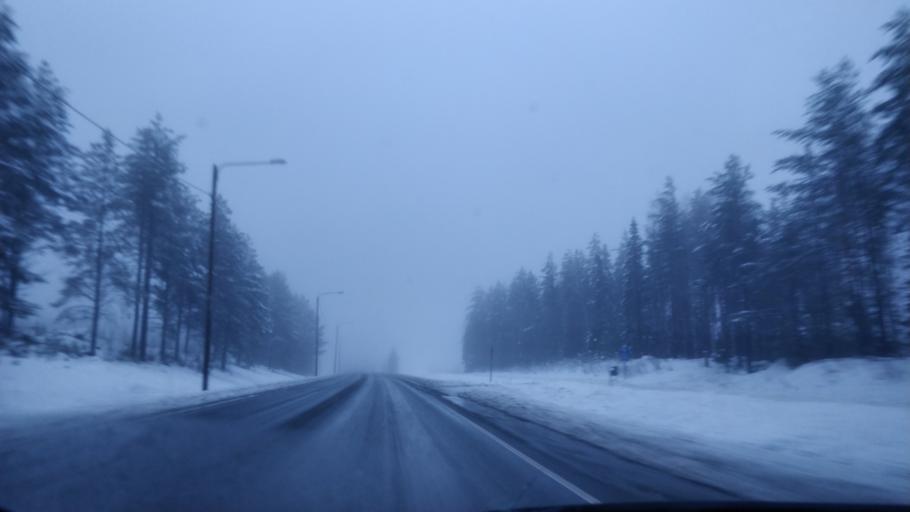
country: FI
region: Lapland
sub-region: Kemi-Tornio
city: Tervola
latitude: 66.1356
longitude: 24.9257
